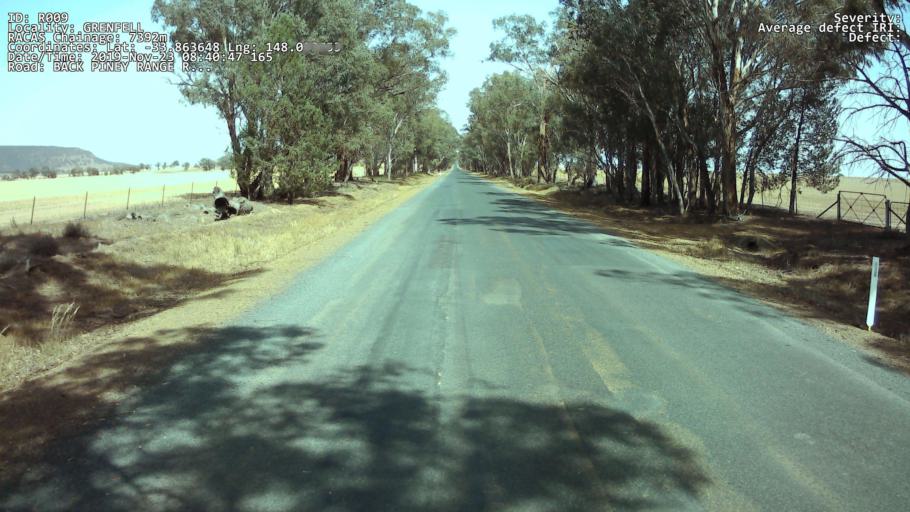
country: AU
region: New South Wales
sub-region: Weddin
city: Grenfell
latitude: -33.8636
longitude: 148.0337
